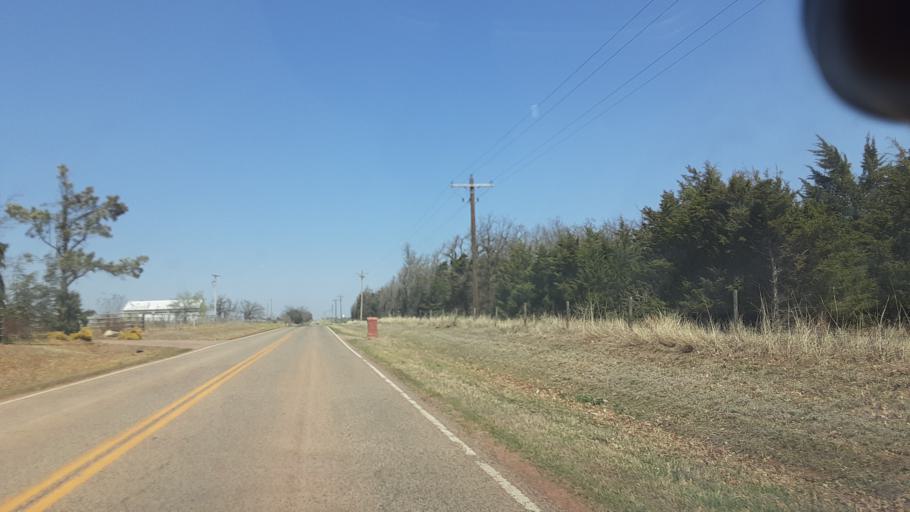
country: US
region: Oklahoma
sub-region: Logan County
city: Guthrie
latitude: 35.8246
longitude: -97.4784
